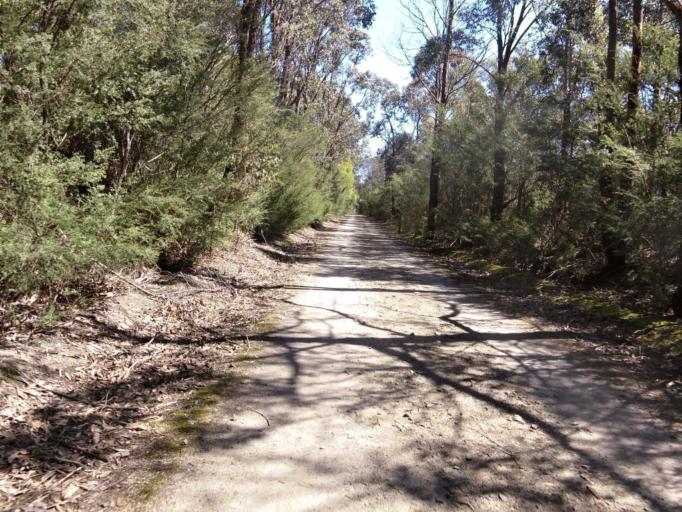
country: AU
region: Victoria
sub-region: Latrobe
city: Moe
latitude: -38.1711
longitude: 146.2998
